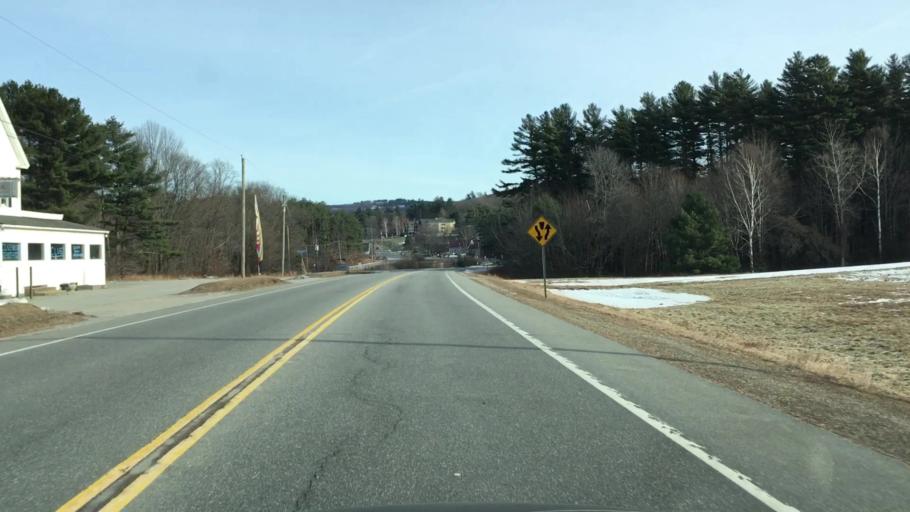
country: US
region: New Hampshire
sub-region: Merrimack County
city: Newbury
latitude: 43.3412
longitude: -72.0751
